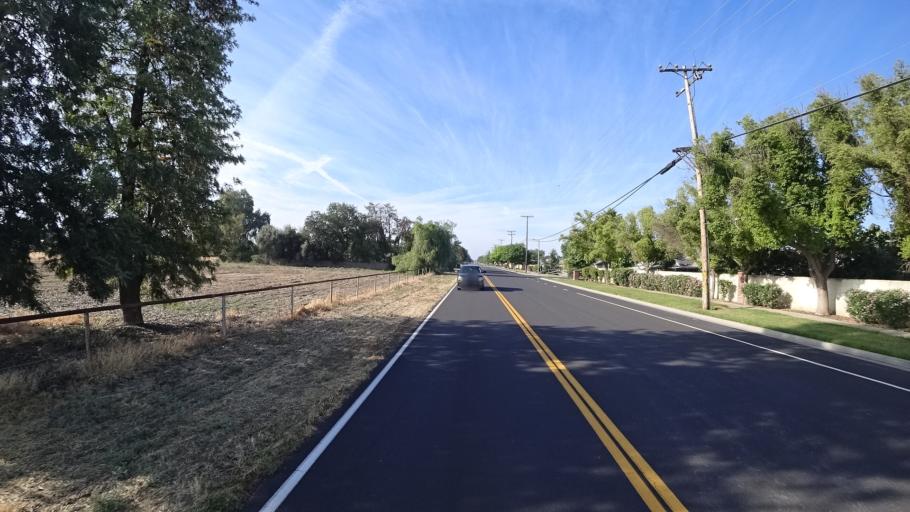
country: US
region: California
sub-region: Kings County
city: Lucerne
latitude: 36.3675
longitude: -119.6460
